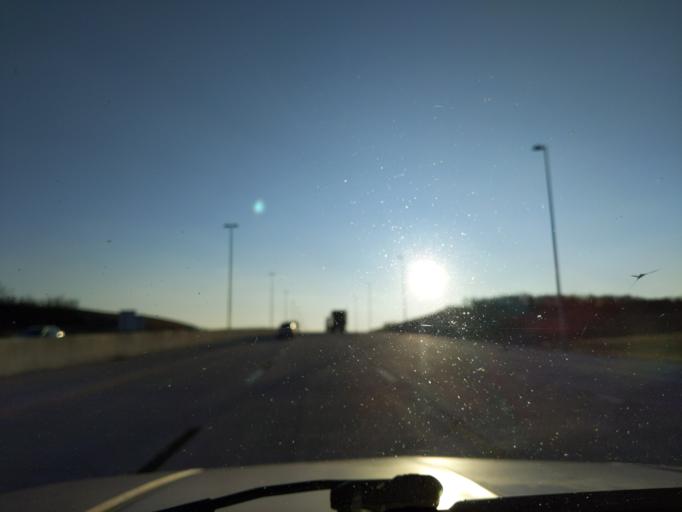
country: US
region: Oklahoma
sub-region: Creek County
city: Kellyville
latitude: 35.9846
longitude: -96.1982
